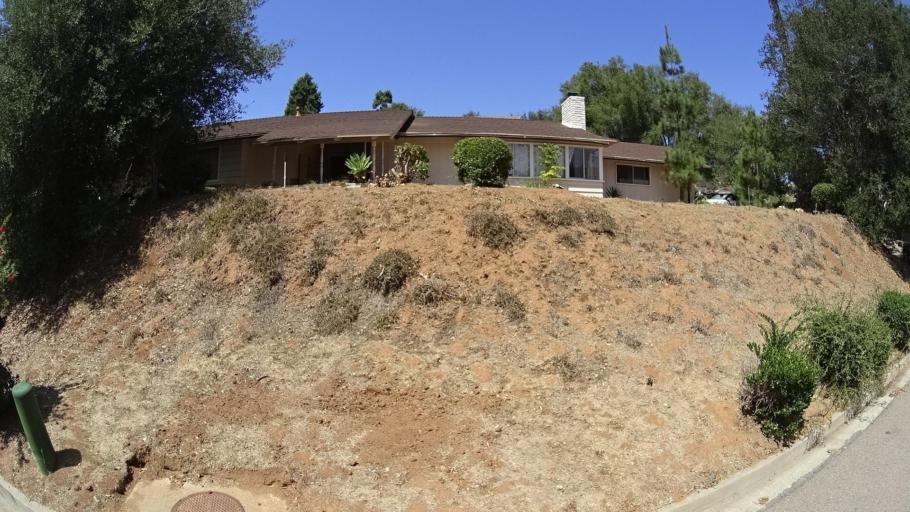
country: US
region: California
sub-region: San Diego County
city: Bonsall
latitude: 33.3405
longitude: -117.1875
